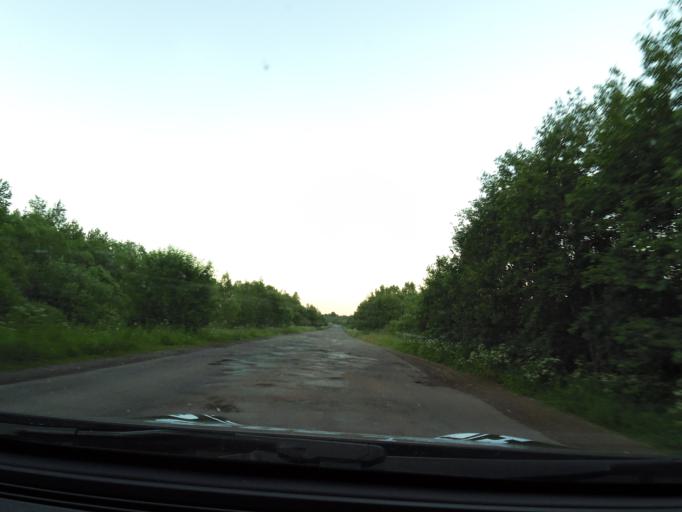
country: RU
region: Leningrad
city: Voznesen'ye
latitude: 60.8488
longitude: 35.5864
